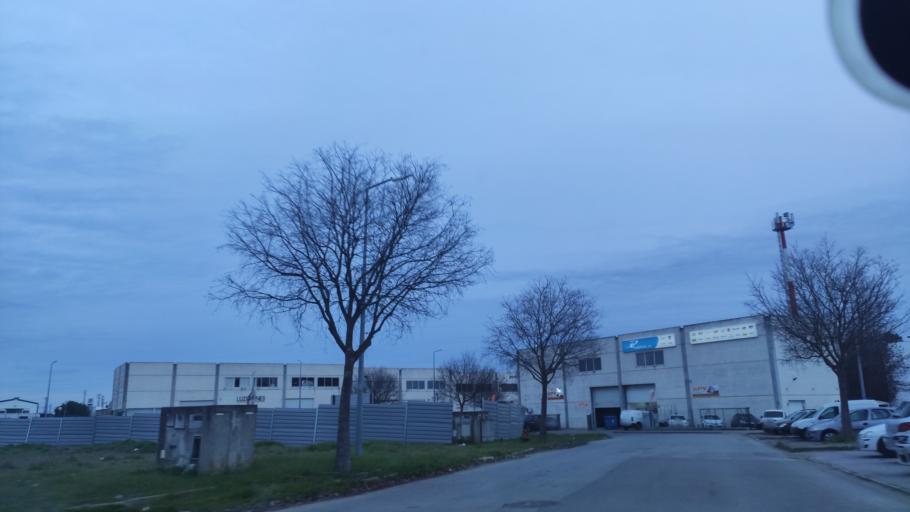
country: PT
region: Beja
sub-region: Beja
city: Beja
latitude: 38.0201
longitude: -7.8536
